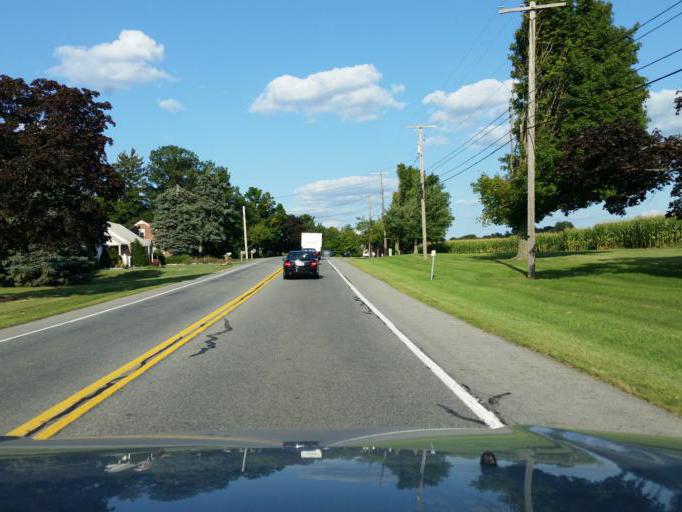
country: US
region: Pennsylvania
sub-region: Dauphin County
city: Palmdale
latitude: 40.2765
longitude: -76.6134
